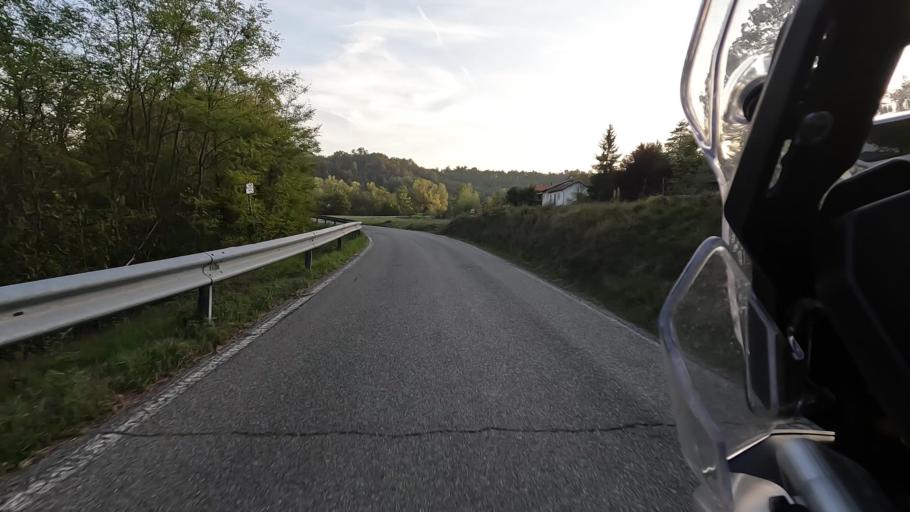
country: IT
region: Liguria
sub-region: Provincia di Savona
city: Mioglia
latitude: 44.5126
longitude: 8.4441
